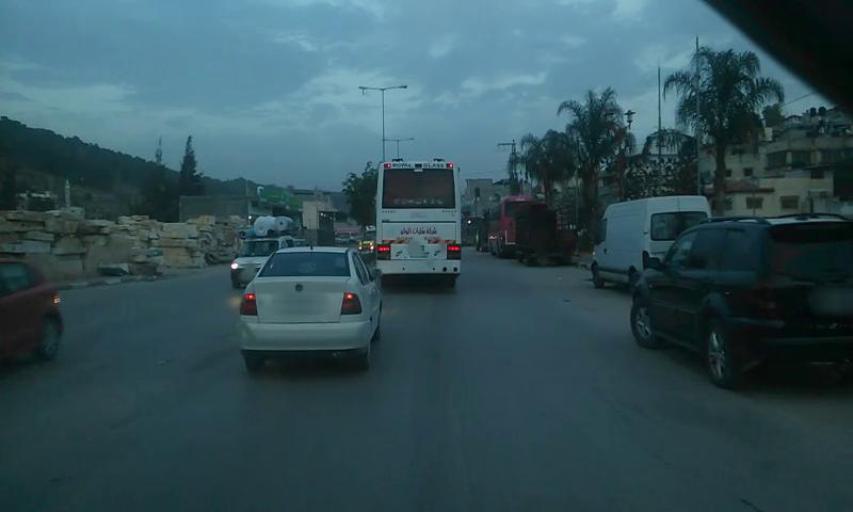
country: PS
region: West Bank
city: Iktabah
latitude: 32.3195
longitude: 35.0554
